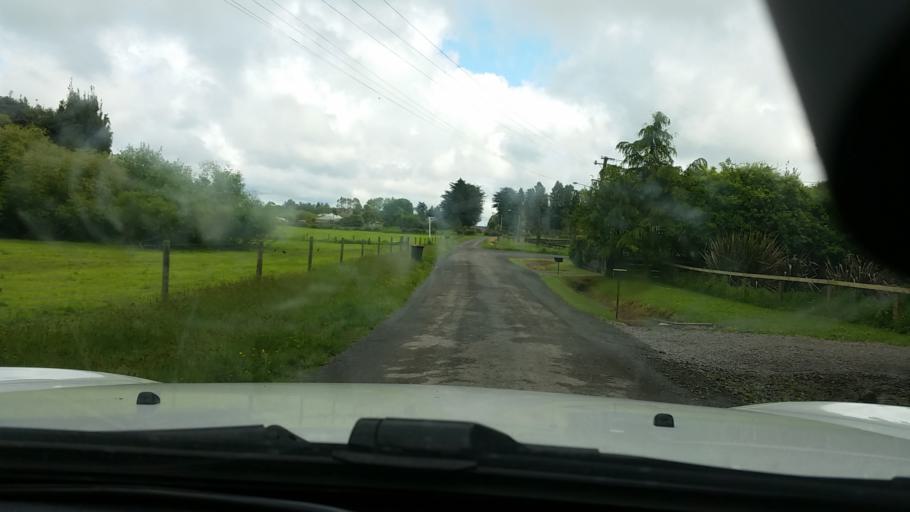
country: NZ
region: Bay of Plenty
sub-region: Rotorua District
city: Rotorua
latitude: -38.1003
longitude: 176.0753
